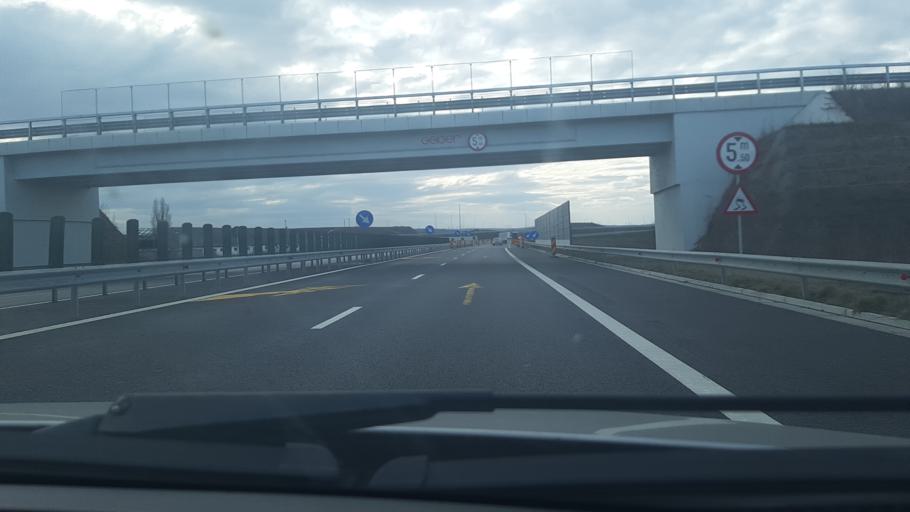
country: RO
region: Mures
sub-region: Comuna Iernut
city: Cipau
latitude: 46.4319
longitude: 24.2768
